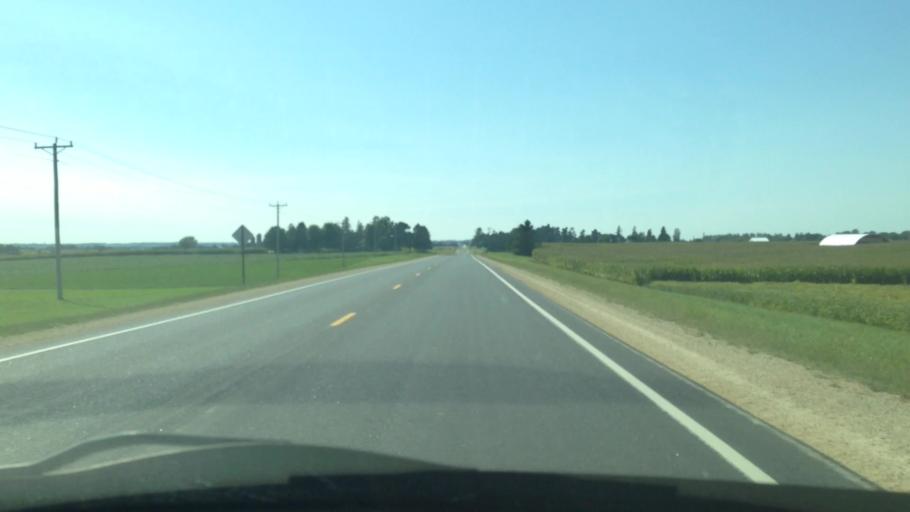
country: US
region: Minnesota
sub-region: Winona County
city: Lewiston
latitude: 43.9697
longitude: -91.8405
